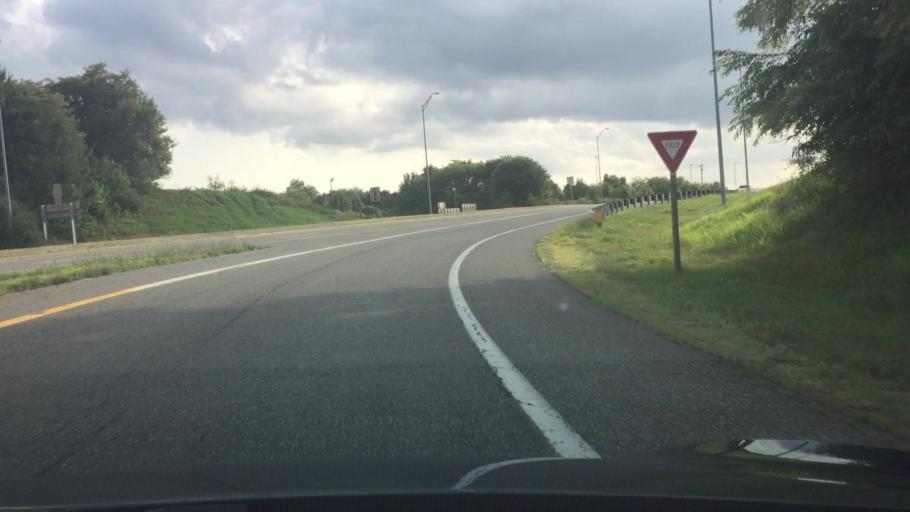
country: US
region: Virginia
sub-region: Montgomery County
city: Merrimac
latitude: 37.1653
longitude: -80.4134
